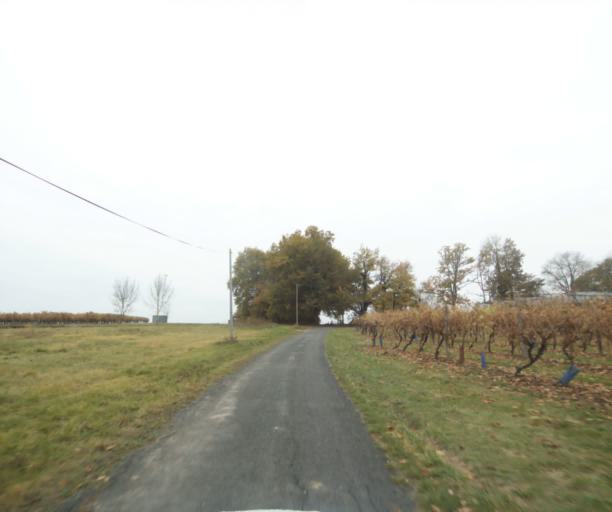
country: FR
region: Poitou-Charentes
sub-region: Departement de la Charente-Maritime
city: Chermignac
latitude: 45.7094
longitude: -0.6825
